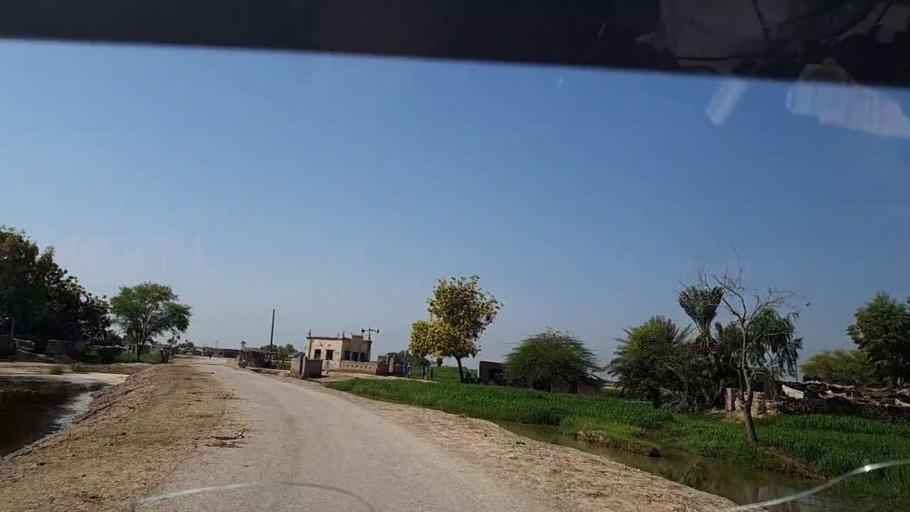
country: PK
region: Sindh
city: Tangwani
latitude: 28.3169
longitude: 69.0941
